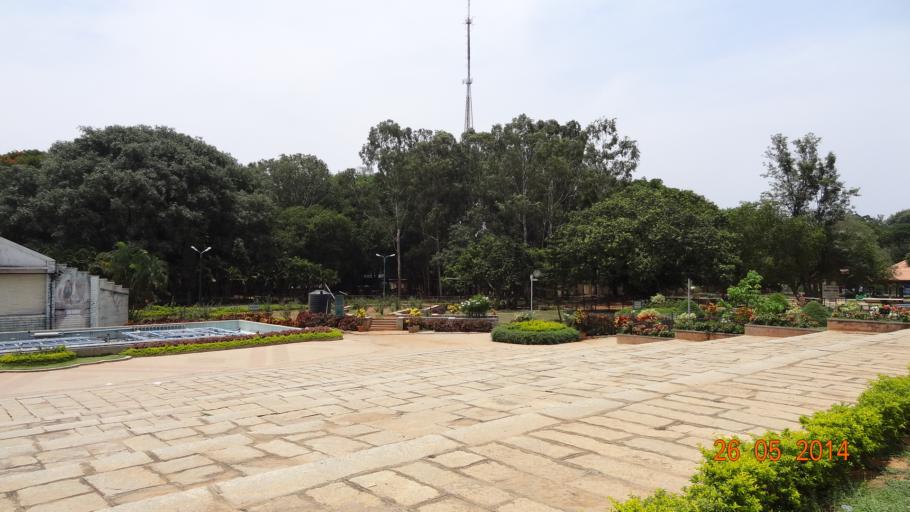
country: IN
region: Karnataka
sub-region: Bangalore Urban
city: Bangalore
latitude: 12.9853
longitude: 77.5916
